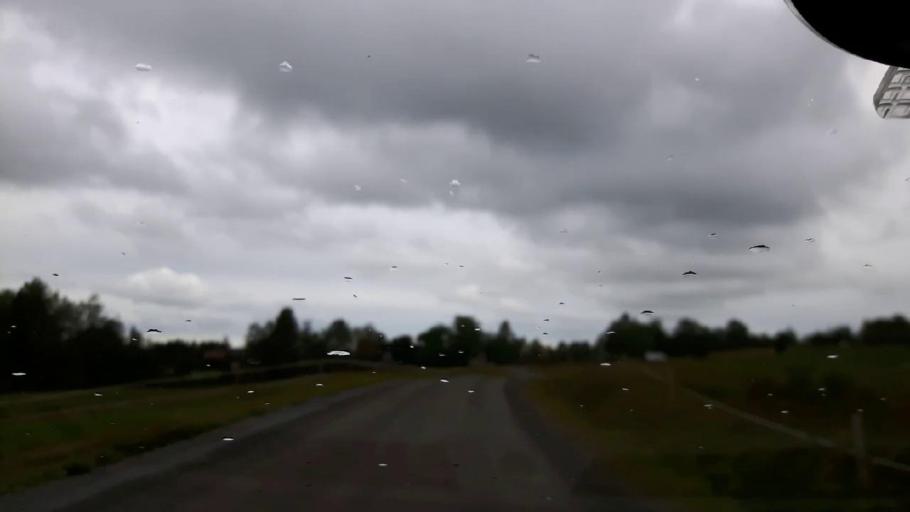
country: SE
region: Jaemtland
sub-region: OEstersunds Kommun
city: Ostersund
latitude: 63.0325
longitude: 14.5779
